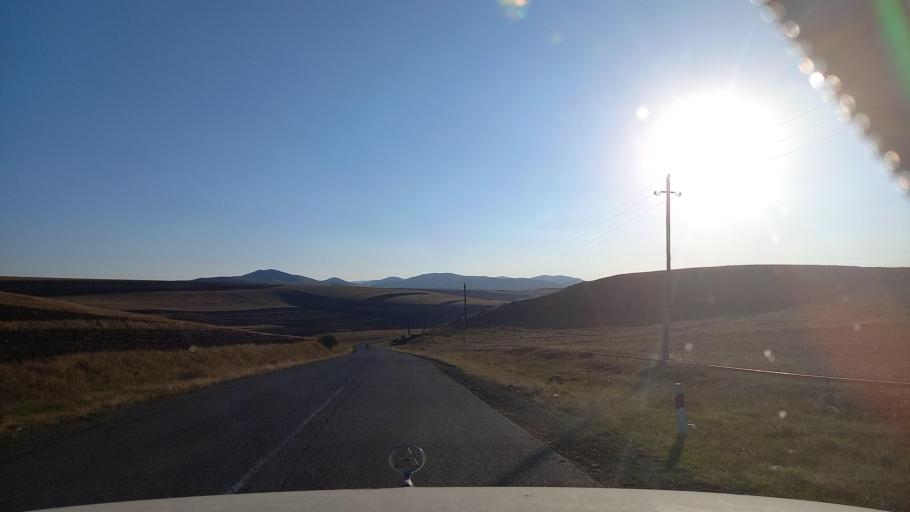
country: AZ
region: Shamkir Rayon
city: Shamkhor
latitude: 40.7660
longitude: 45.9363
